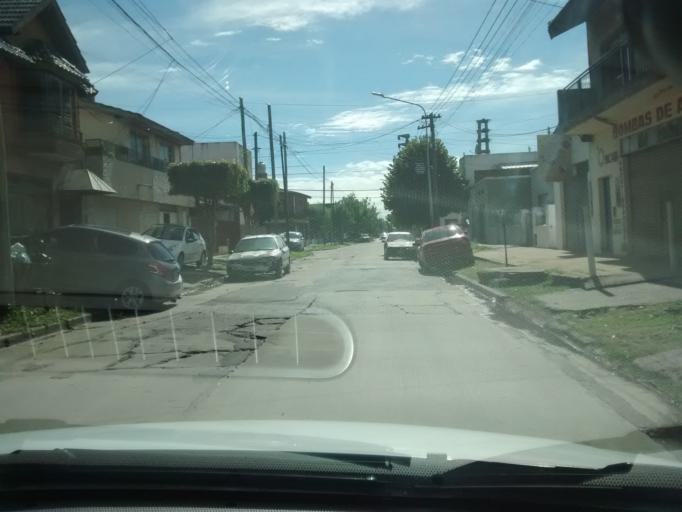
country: AR
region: Buenos Aires
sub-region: Partido de Moron
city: Moron
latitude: -34.6649
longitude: -58.6077
